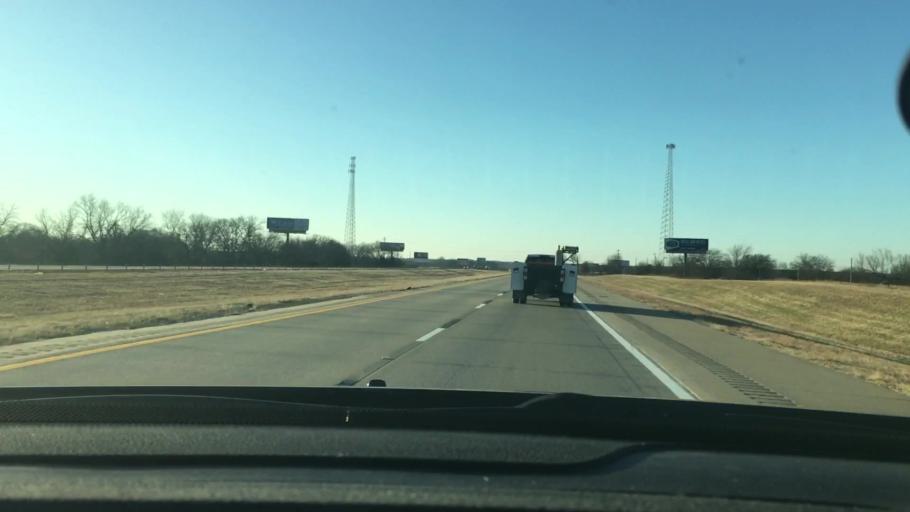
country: US
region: Oklahoma
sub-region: Carter County
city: Ardmore
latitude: 34.2790
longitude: -97.1611
